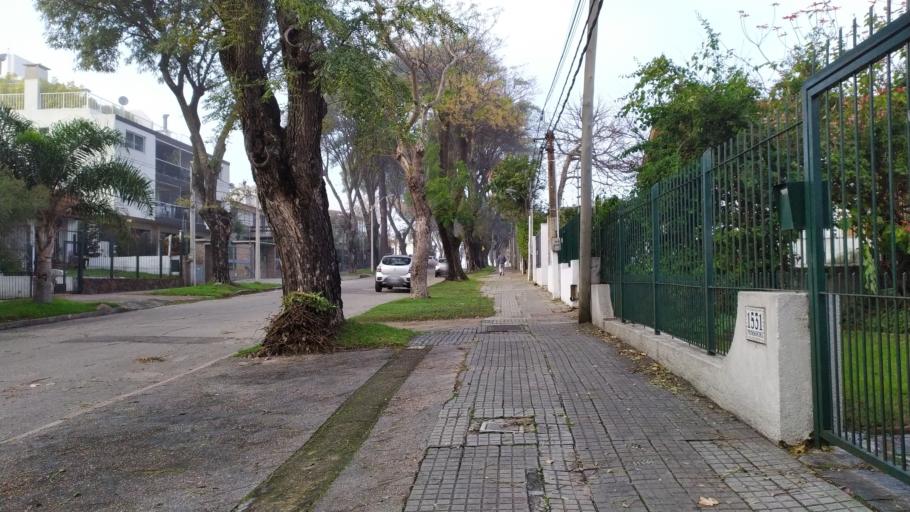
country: UY
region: Canelones
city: Paso de Carrasco
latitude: -34.8928
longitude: -56.0966
